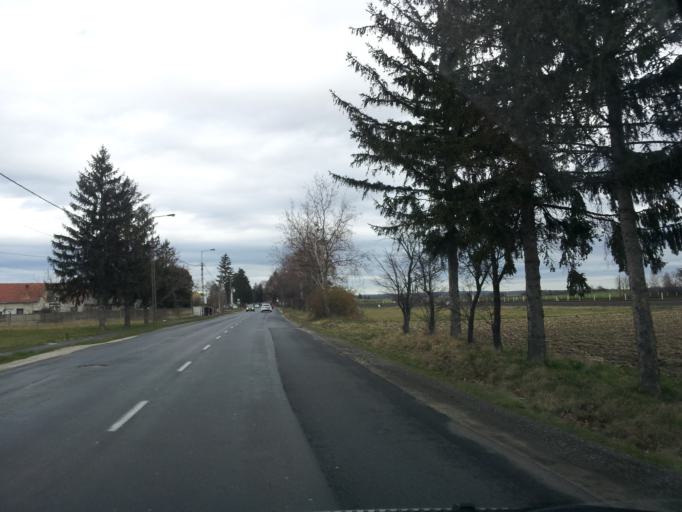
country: HU
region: Vas
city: Gencsapati
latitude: 47.3203
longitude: 16.5866
